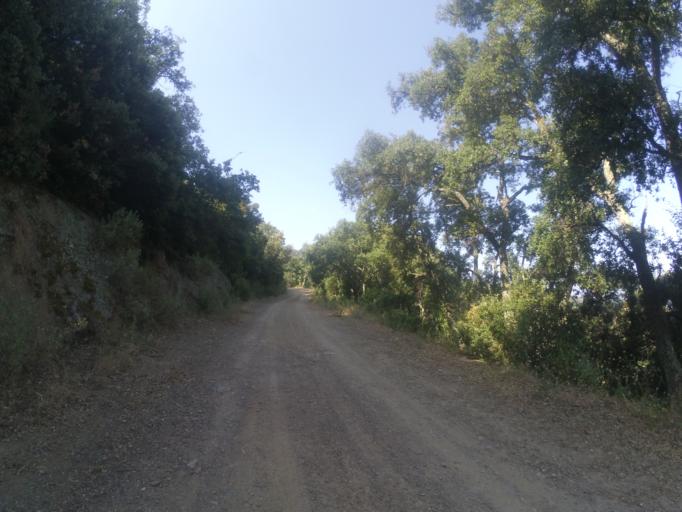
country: FR
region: Languedoc-Roussillon
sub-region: Departement des Pyrenees-Orientales
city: Ille-sur-Tet
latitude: 42.6512
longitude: 2.6437
